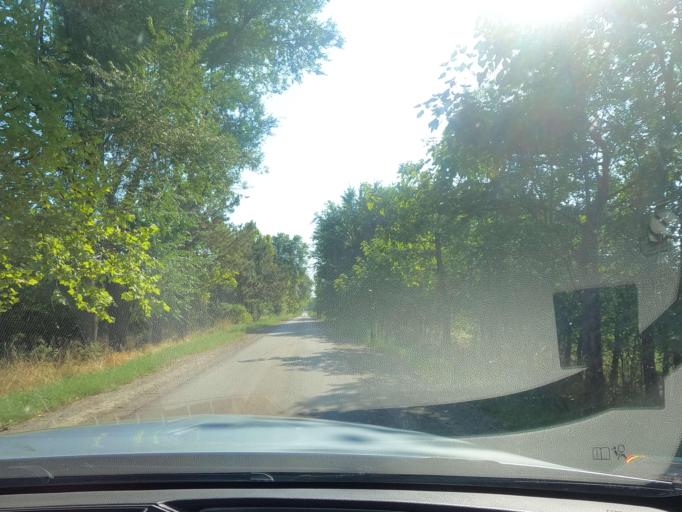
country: RS
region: Autonomna Pokrajina Vojvodina
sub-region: Juznobacki Okrug
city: Becej
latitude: 45.6643
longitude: 19.9081
